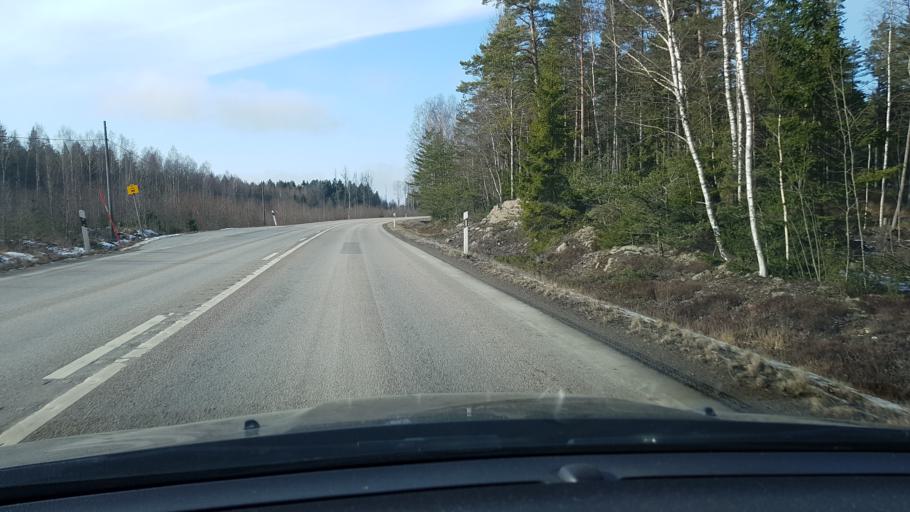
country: SE
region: Uppsala
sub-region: Heby Kommun
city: Morgongava
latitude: 59.8985
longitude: 17.0934
